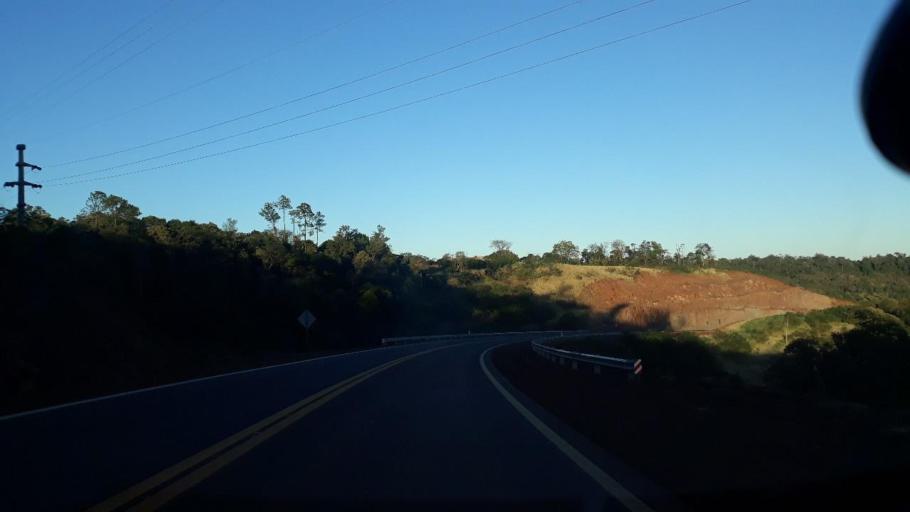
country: AR
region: Misiones
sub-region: Departamento de San Pedro
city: San Pedro
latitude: -26.5385
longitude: -53.9417
